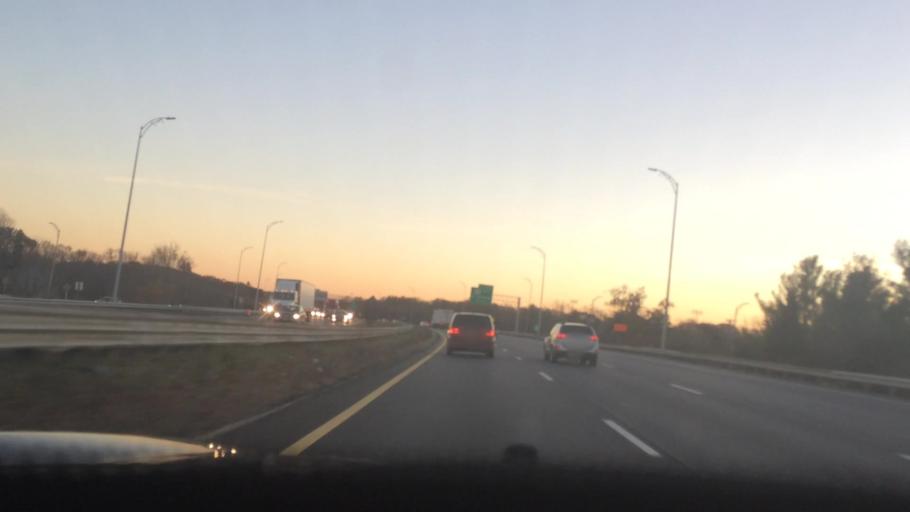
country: US
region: Massachusetts
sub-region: Essex County
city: North Andover
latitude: 42.6973
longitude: -71.1422
